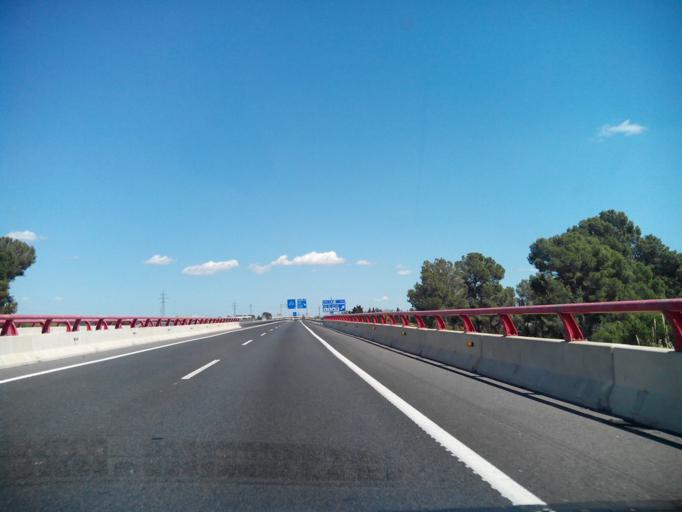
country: ES
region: Catalonia
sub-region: Provincia de Tarragona
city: Cambrils
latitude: 41.0782
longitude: 1.0225
